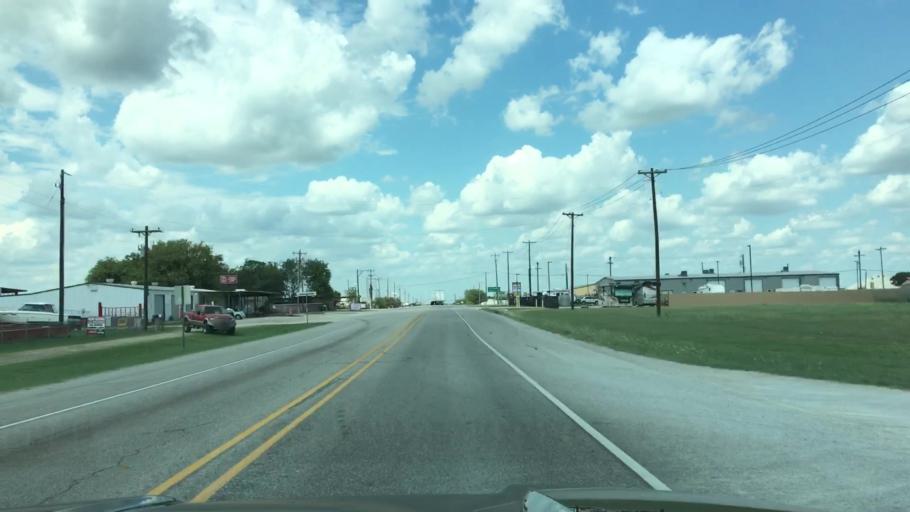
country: US
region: Texas
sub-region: Tarrant County
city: Pecan Acres
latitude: 32.9481
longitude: -97.4208
